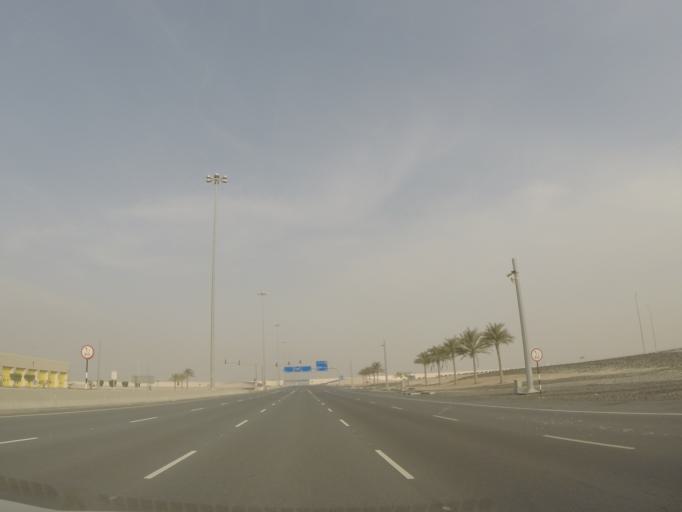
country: AE
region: Abu Dhabi
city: Abu Dhabi
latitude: 24.7750
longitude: 54.7126
